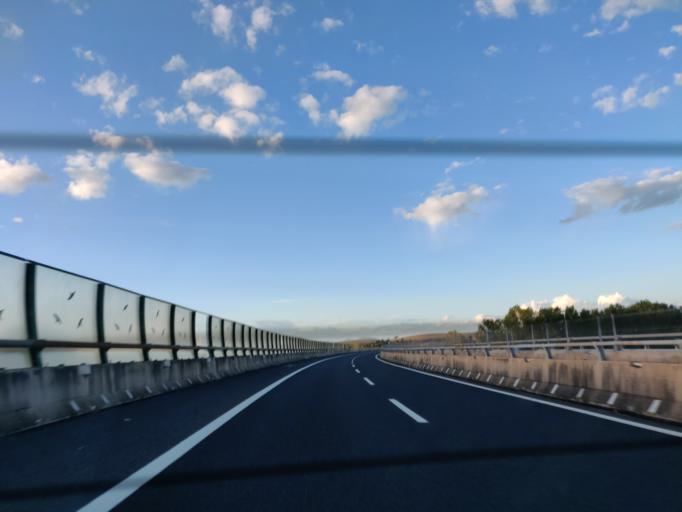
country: IT
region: Tuscany
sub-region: Provincia di Livorno
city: Rosignano Marittimo
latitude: 43.4350
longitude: 10.4863
